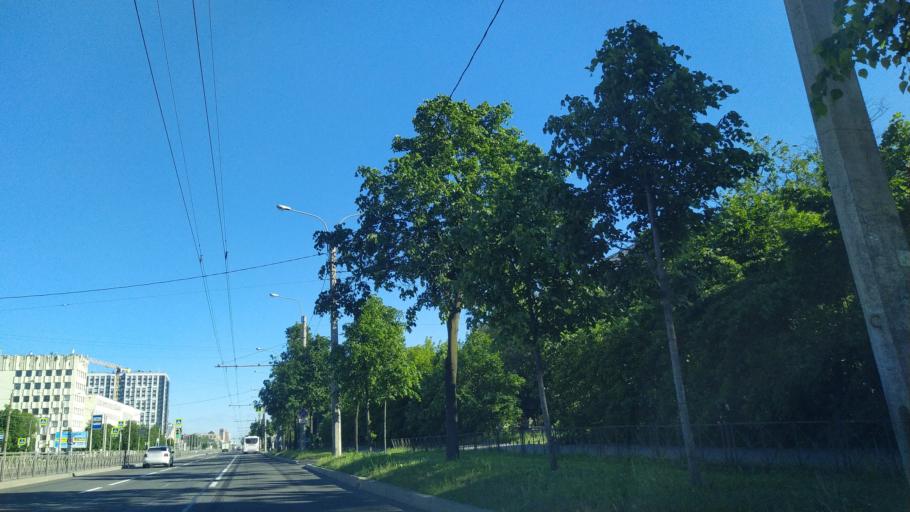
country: RU
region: St.-Petersburg
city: Kupchino
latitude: 59.8887
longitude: 30.3620
